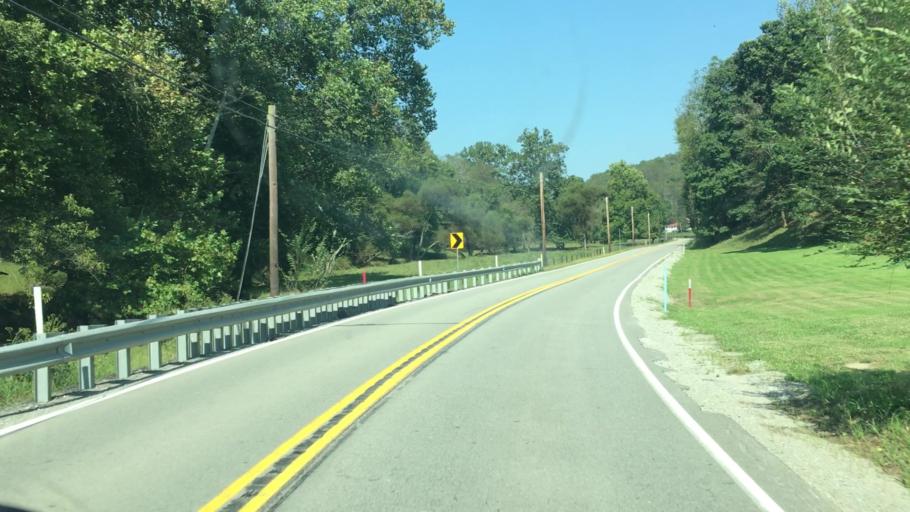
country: US
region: Pennsylvania
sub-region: Greene County
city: Waynesburg
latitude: 39.9422
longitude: -80.2891
